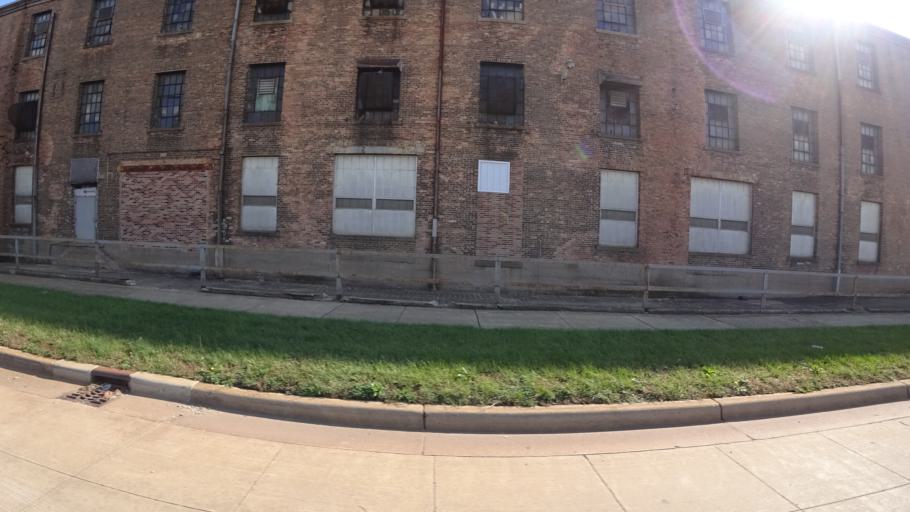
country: US
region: Michigan
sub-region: Saint Joseph County
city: Three Rivers
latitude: 41.9367
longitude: -85.6297
